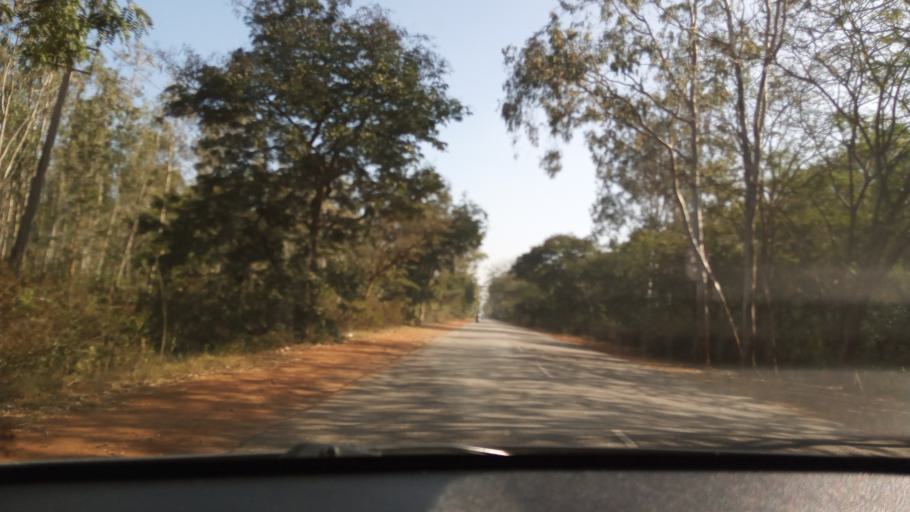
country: IN
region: Karnataka
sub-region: Bangalore Rural
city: Devanhalli
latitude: 13.2713
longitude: 77.7486
